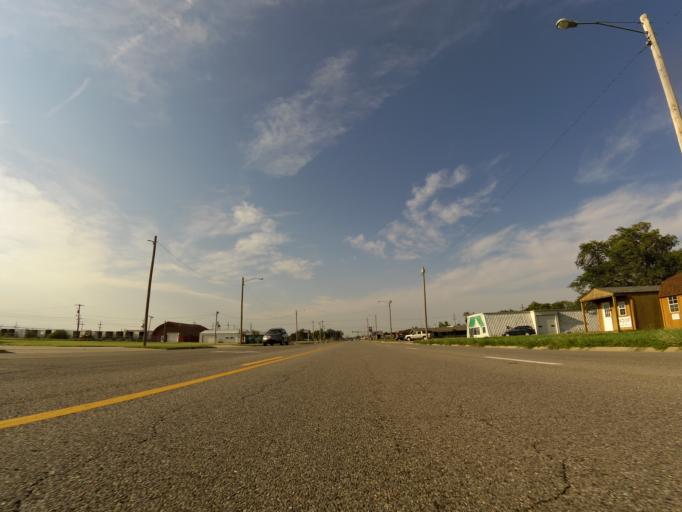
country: US
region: Kansas
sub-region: Reno County
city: South Hutchinson
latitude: 38.0257
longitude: -97.9402
